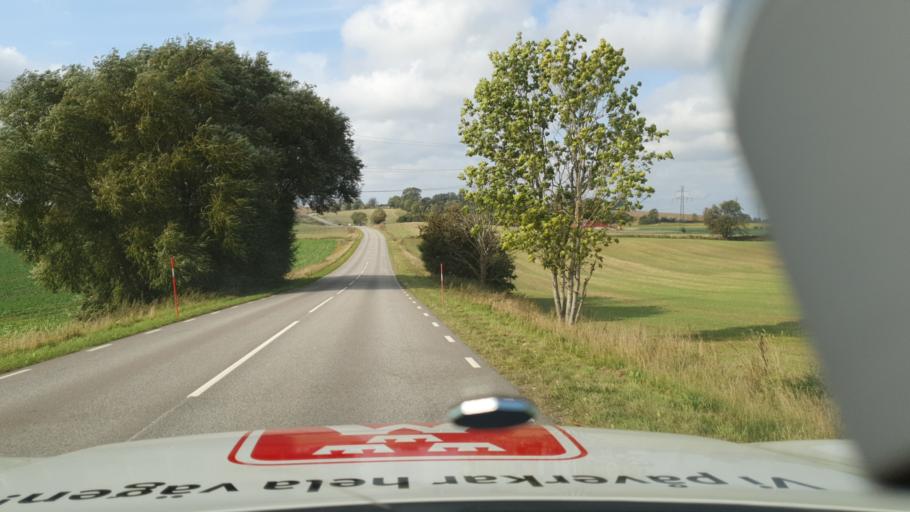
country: SE
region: Skane
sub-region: Svedala Kommun
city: Svedala
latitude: 55.4969
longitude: 13.1749
